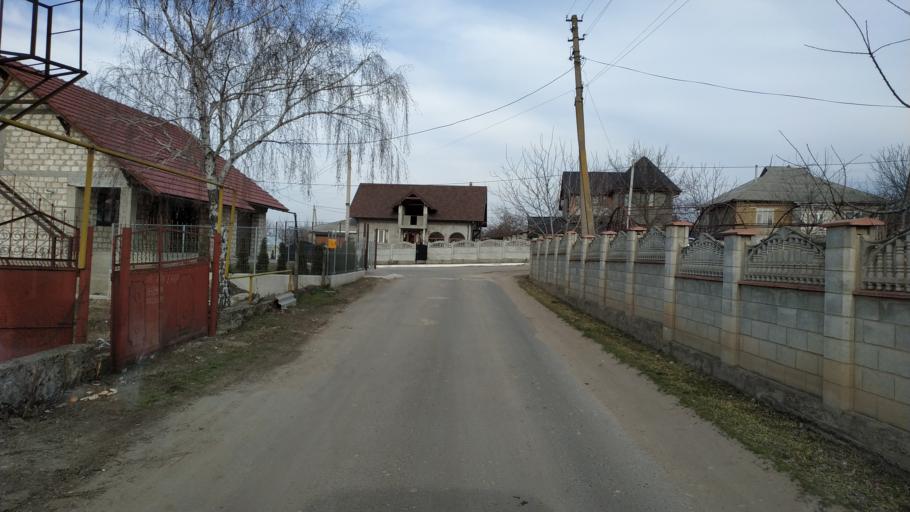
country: MD
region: Chisinau
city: Vatra
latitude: 46.9861
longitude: 28.6696
